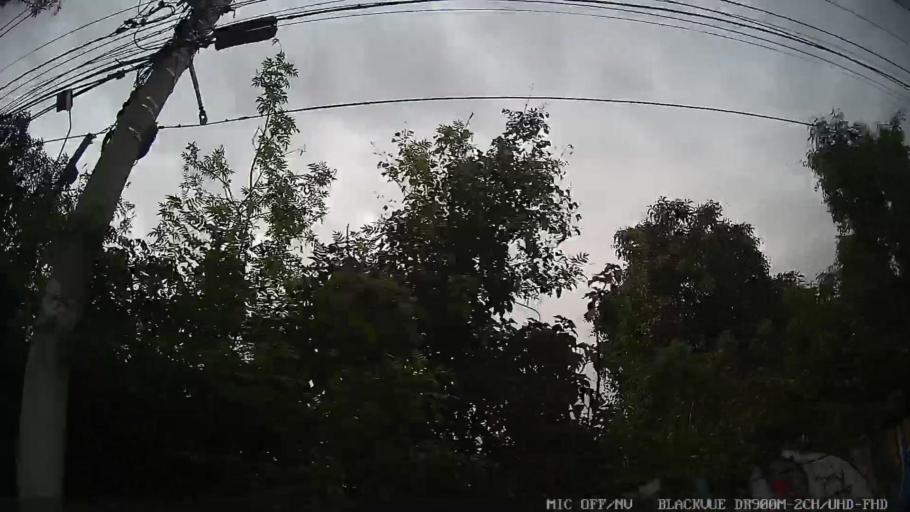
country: BR
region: Sao Paulo
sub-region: Osasco
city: Osasco
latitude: -23.4693
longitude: -46.7093
